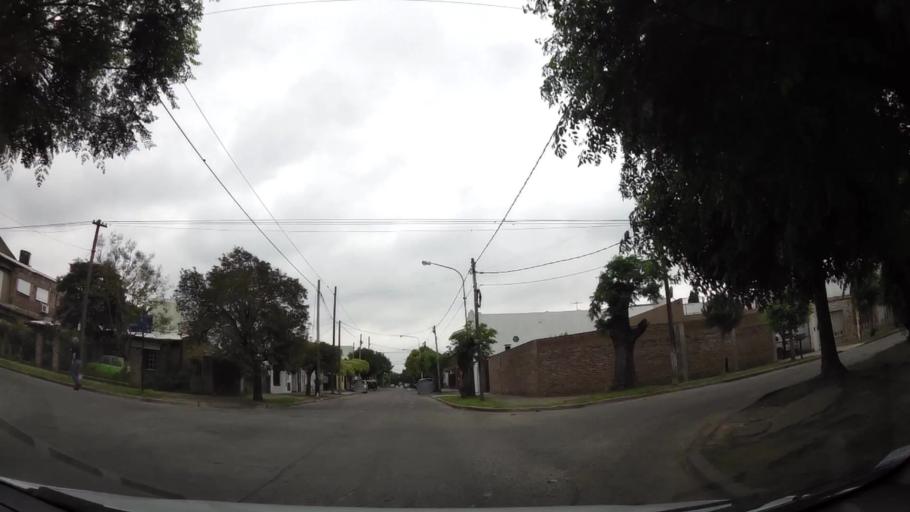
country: AR
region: Buenos Aires
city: San Justo
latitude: -34.7059
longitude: -58.5185
